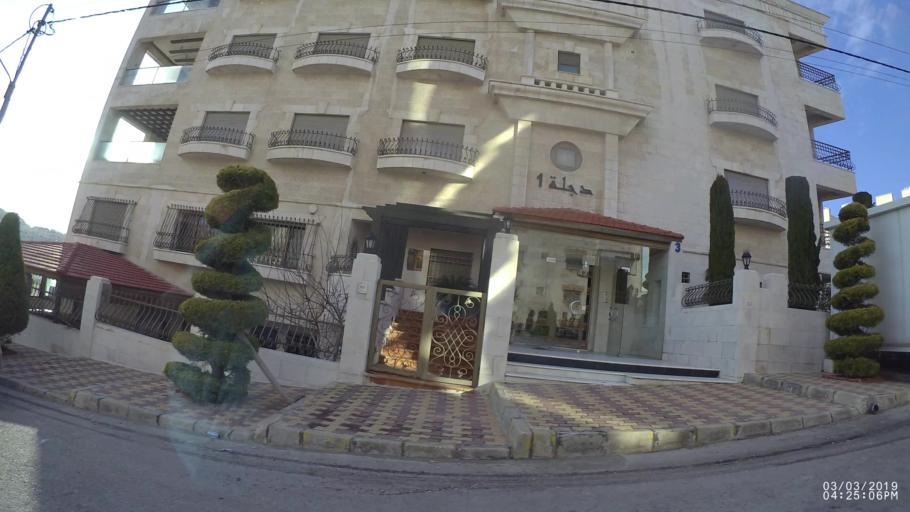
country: JO
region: Amman
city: Al Jubayhah
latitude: 31.9797
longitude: 35.8849
